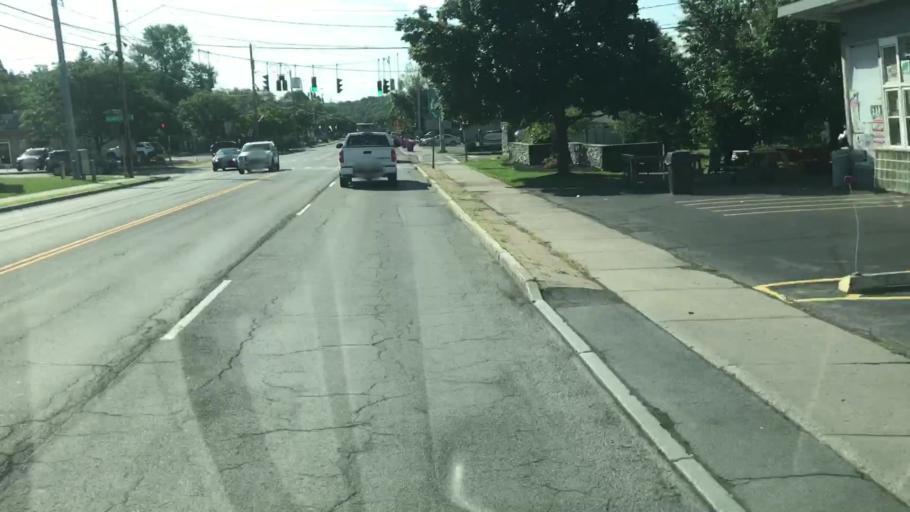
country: US
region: New York
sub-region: Onondaga County
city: Manlius
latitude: 43.0048
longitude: -75.9832
